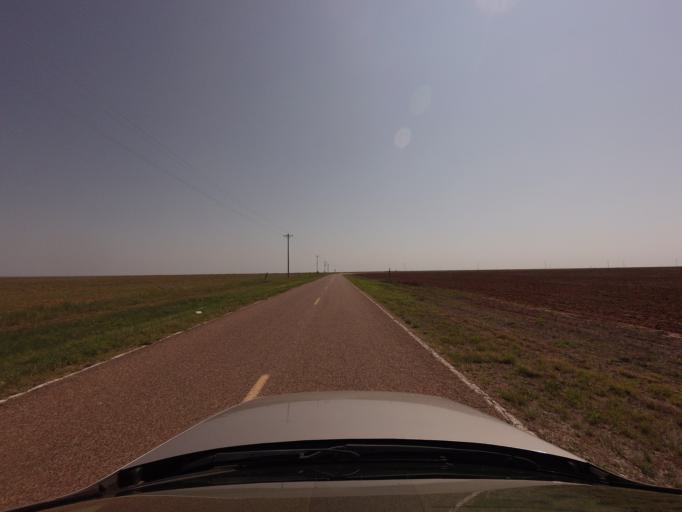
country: US
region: New Mexico
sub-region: Curry County
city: Cannon Air Force Base
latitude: 34.6327
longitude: -103.3058
